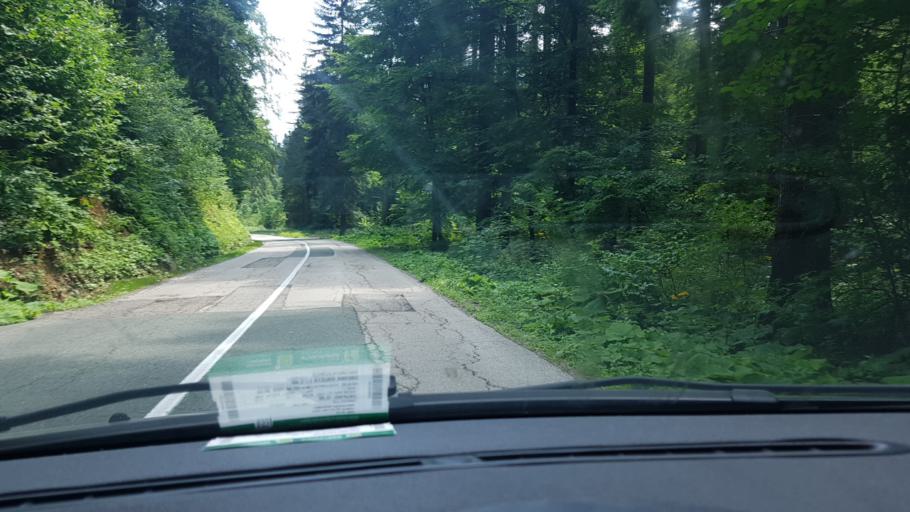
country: HR
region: Primorsko-Goranska
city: Hreljin
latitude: 45.3360
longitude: 14.6763
